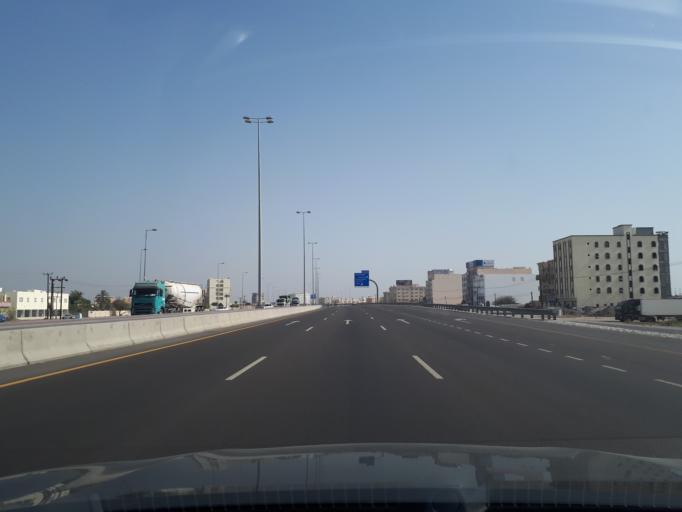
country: OM
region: Al Batinah
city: Al Liwa'
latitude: 24.4369
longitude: 56.6073
